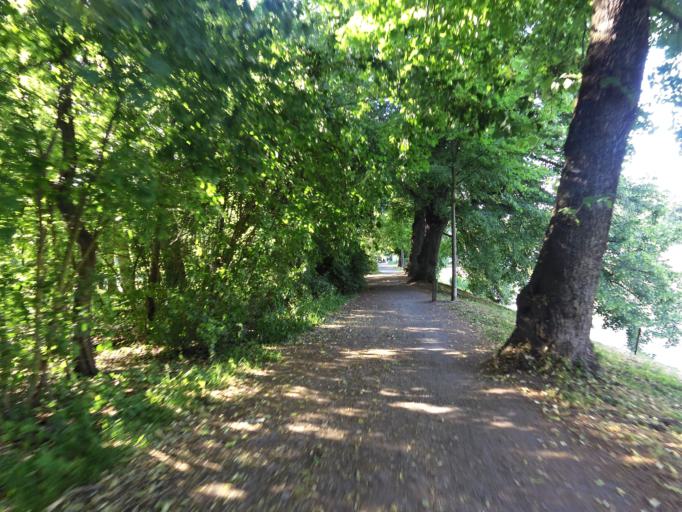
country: DE
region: Saxony
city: Leipzig
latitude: 51.3291
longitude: 12.3543
